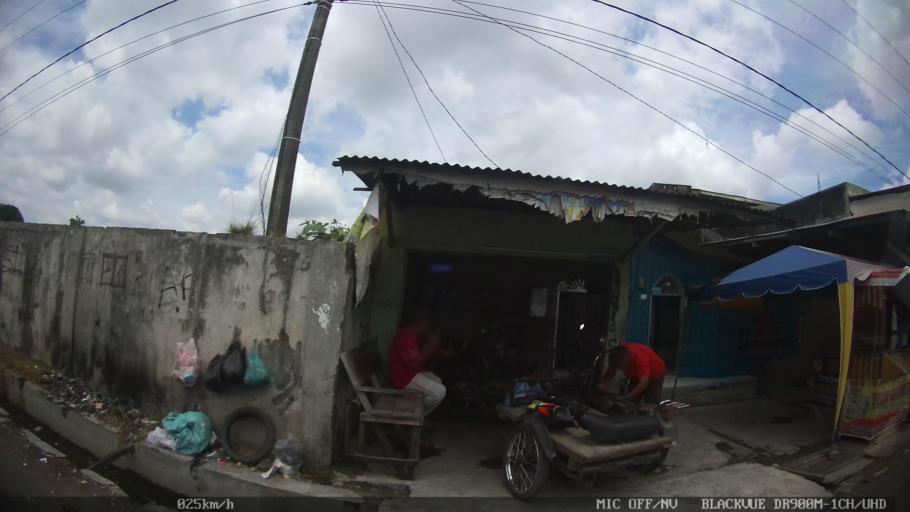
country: ID
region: North Sumatra
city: Medan
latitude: 3.6157
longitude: 98.7481
